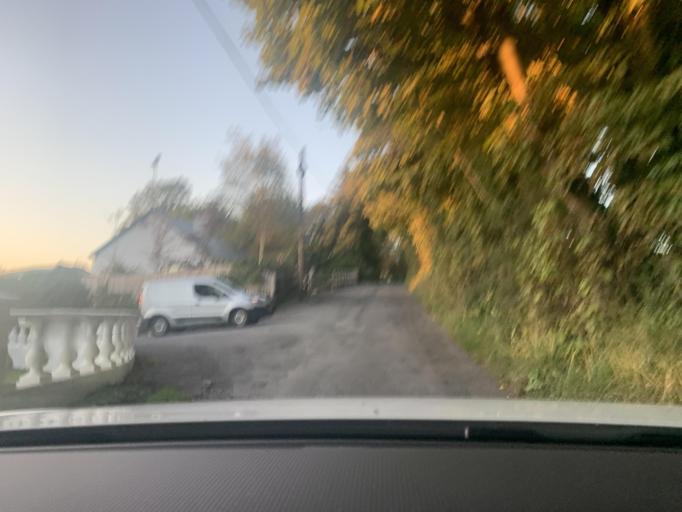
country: IE
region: Connaught
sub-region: Sligo
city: Sligo
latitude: 54.2751
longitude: -8.4264
